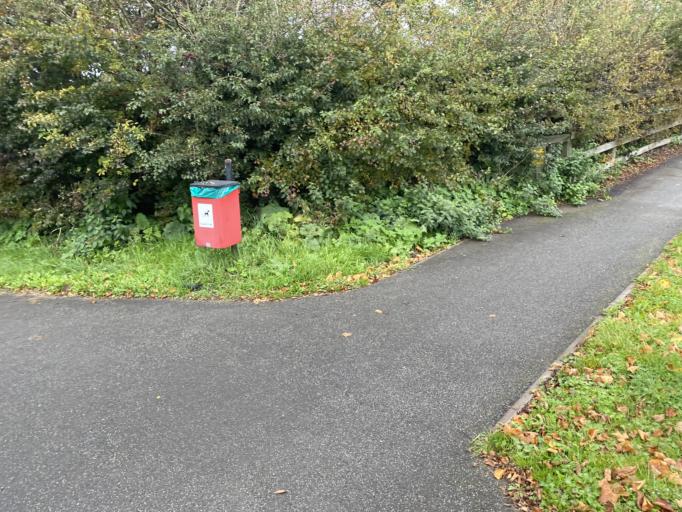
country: GB
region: England
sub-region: Cheshire West and Chester
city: Hoole
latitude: 53.2143
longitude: -2.8962
